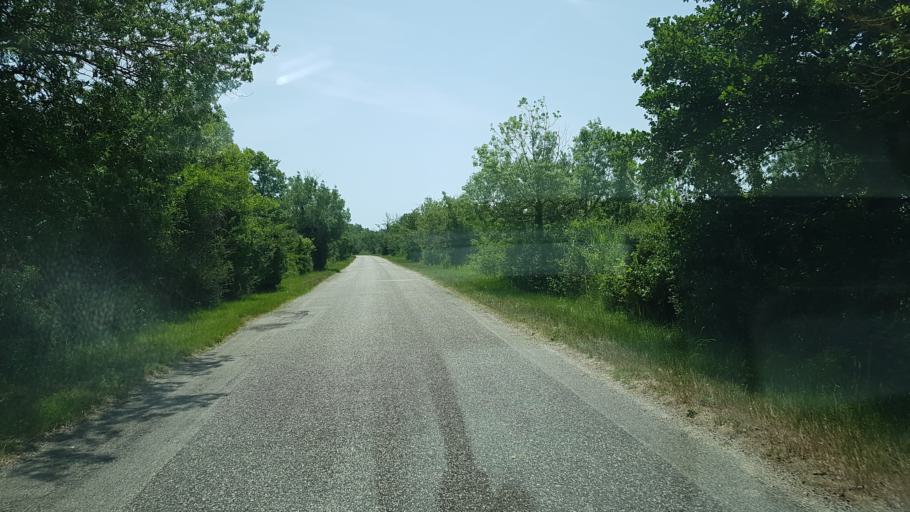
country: FR
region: Provence-Alpes-Cote d'Azur
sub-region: Departement des Bouches-du-Rhone
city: Port-Saint-Louis-du-Rhone
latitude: 43.4597
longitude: 4.6580
